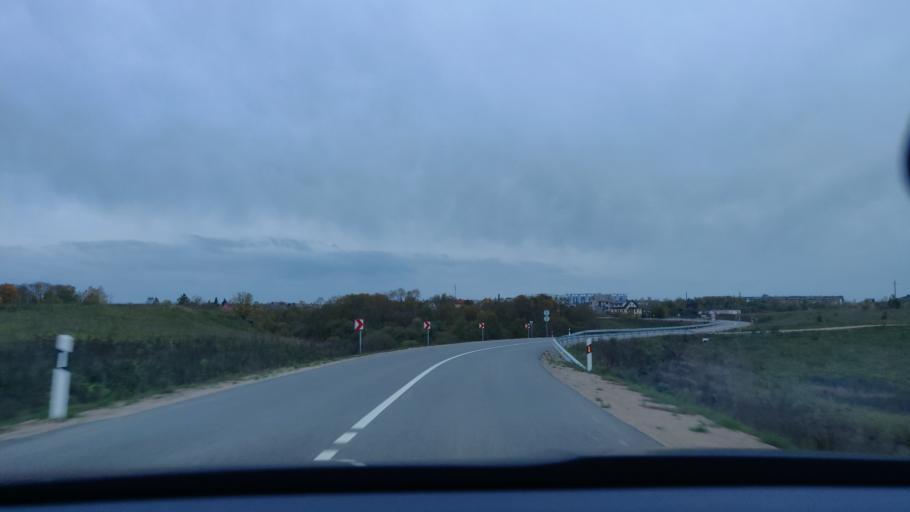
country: LT
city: Trakai
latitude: 54.6076
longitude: 24.9945
